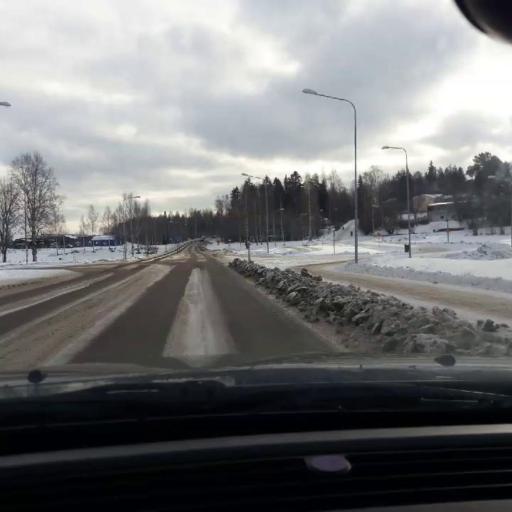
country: SE
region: Gaevleborg
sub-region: Bollnas Kommun
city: Bollnas
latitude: 61.3385
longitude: 16.3891
